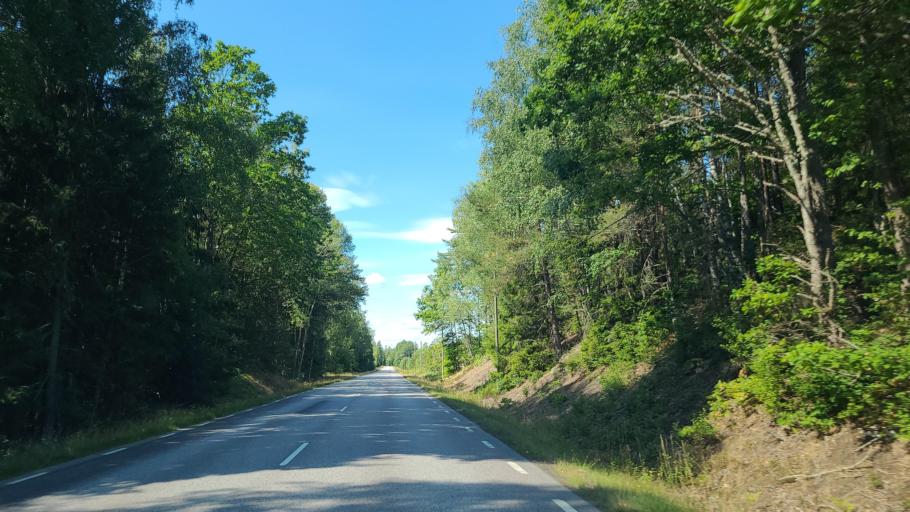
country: SE
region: Kalmar
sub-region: Nybro Kommun
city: Nybro
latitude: 56.5630
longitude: 15.7818
